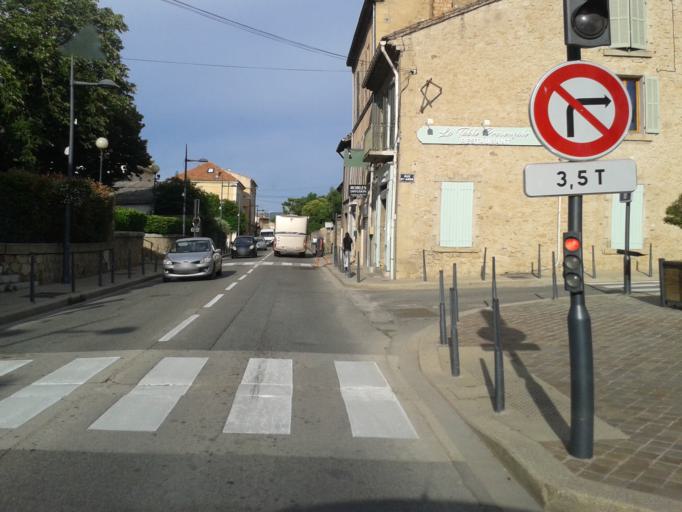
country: FR
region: Provence-Alpes-Cote d'Azur
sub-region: Departement des Bouches-du-Rhone
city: Peyrolles-en-Provence
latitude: 43.6464
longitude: 5.5836
